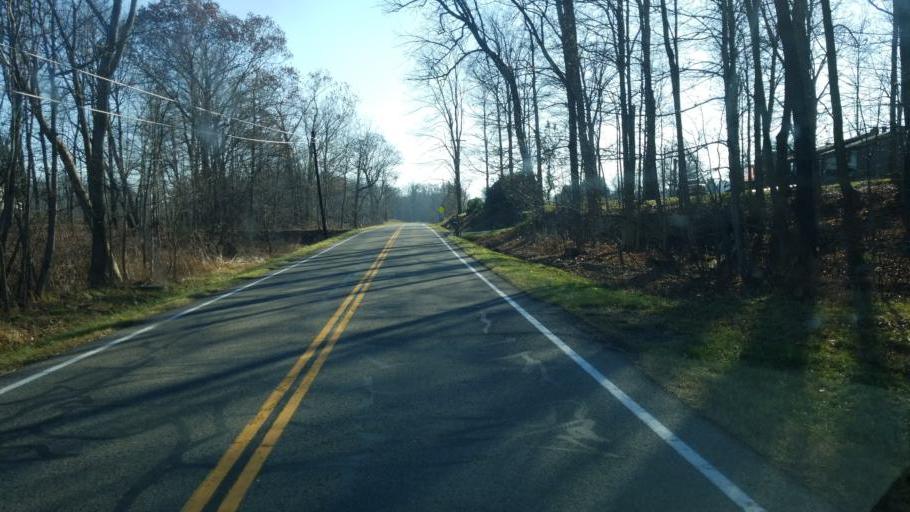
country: US
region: Ohio
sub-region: Geauga County
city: Bainbridge
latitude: 41.4245
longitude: -81.2479
